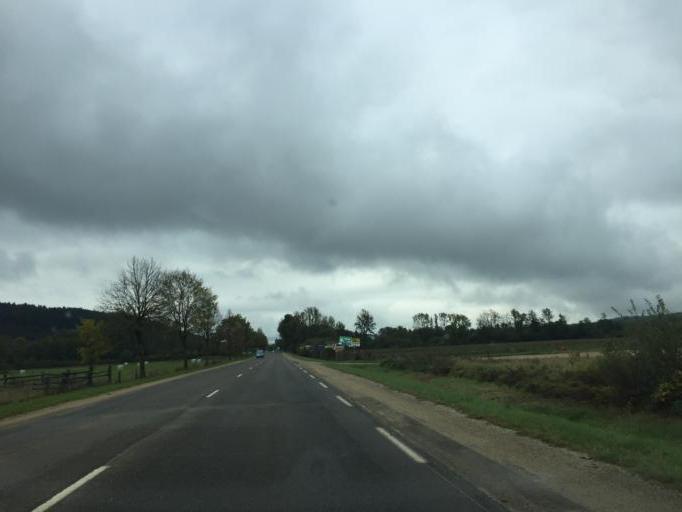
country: FR
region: Franche-Comte
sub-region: Departement du Jura
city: Orgelet
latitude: 46.5407
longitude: 5.6010
